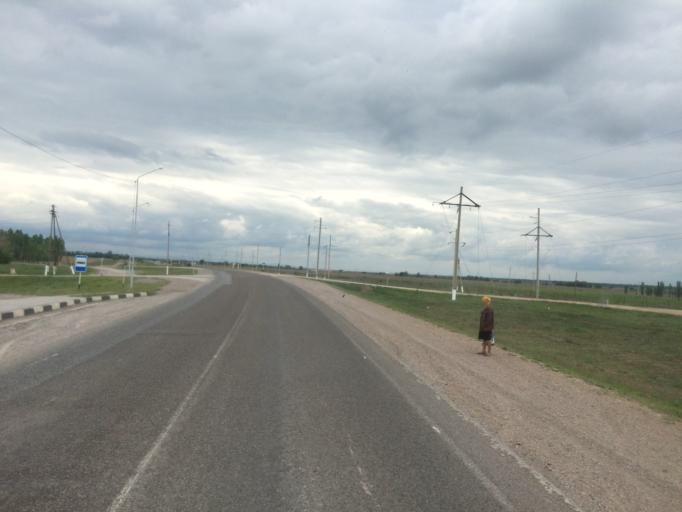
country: KG
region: Chuy
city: Sokuluk
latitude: 43.2468
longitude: 74.2990
